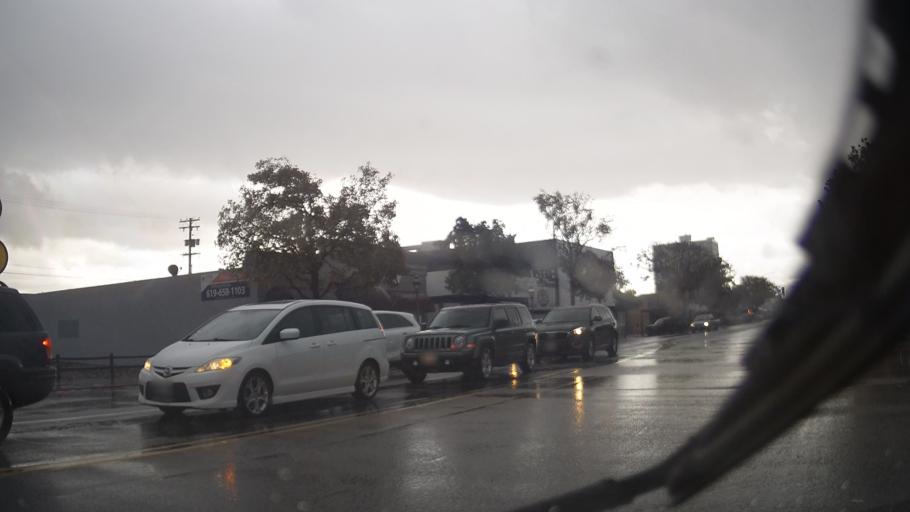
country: US
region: California
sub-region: San Diego County
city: Chula Vista
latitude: 32.6446
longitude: -117.0813
